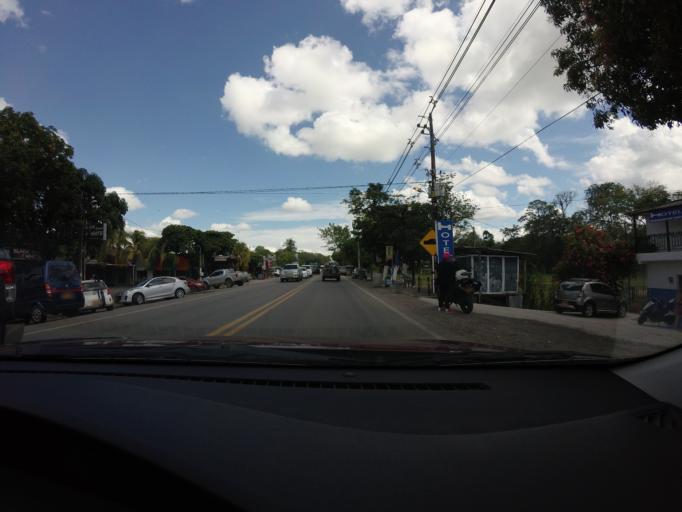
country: CO
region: Antioquia
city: Puerto Triunfo
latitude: 5.8987
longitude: -74.7338
